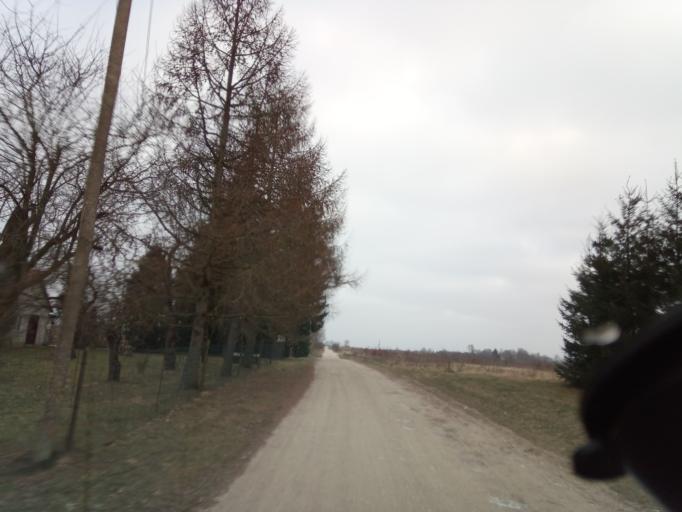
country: LT
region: Alytaus apskritis
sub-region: Alytaus rajonas
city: Daugai
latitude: 54.3734
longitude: 24.4455
